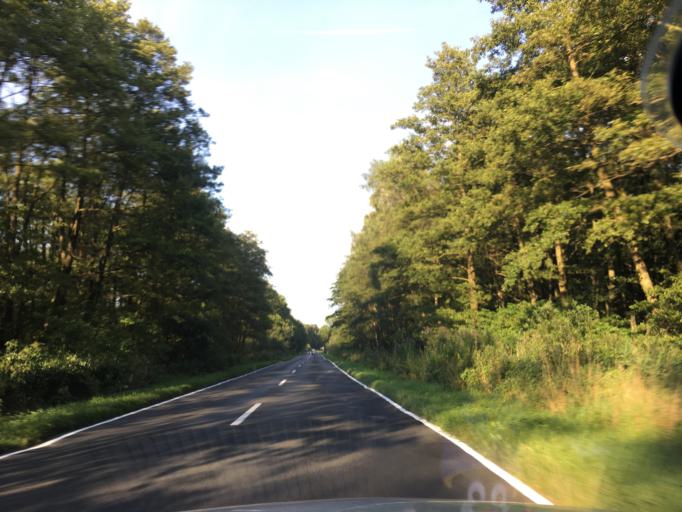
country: PL
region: West Pomeranian Voivodeship
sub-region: Powiat gryficki
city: Pobierowo
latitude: 54.0409
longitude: 14.8649
